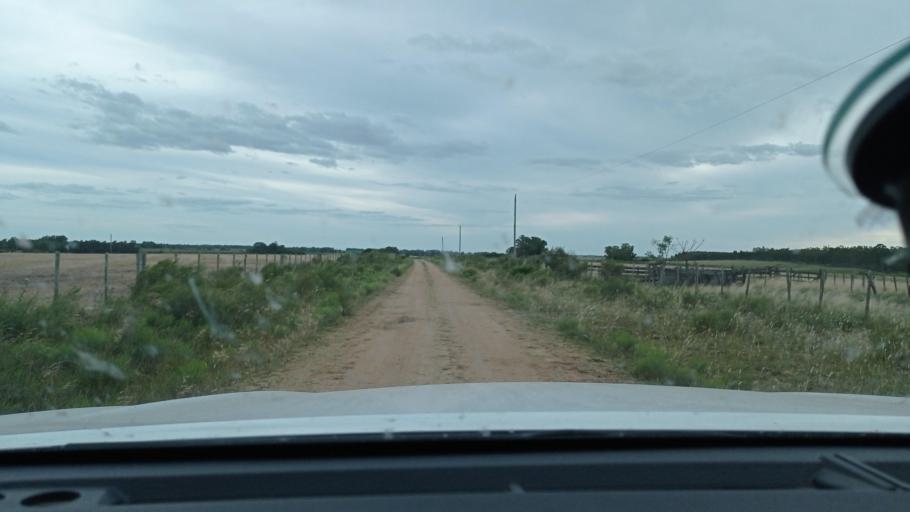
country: UY
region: Florida
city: Casupa
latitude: -34.1370
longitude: -55.8023
